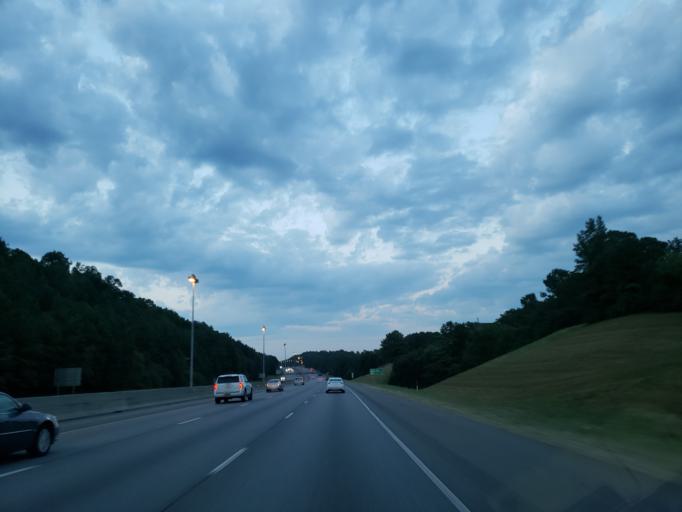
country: US
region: Alabama
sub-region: Jefferson County
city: Cahaba Heights
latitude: 33.4500
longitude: -86.7216
